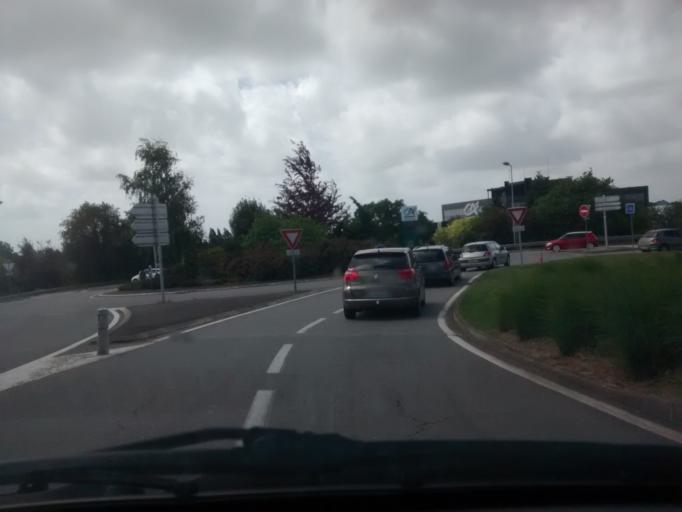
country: FR
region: Brittany
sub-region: Departement du Morbihan
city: Plescop
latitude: 47.6599
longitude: -2.7943
